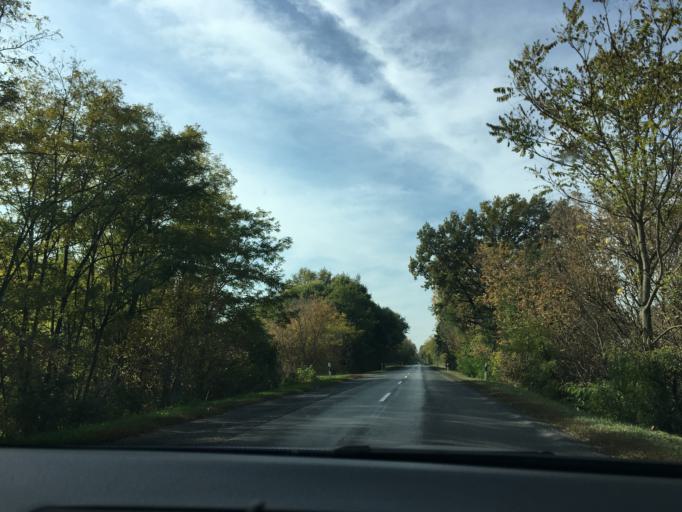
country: HU
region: Hajdu-Bihar
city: Hajdusamson
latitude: 47.5256
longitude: 21.7511
